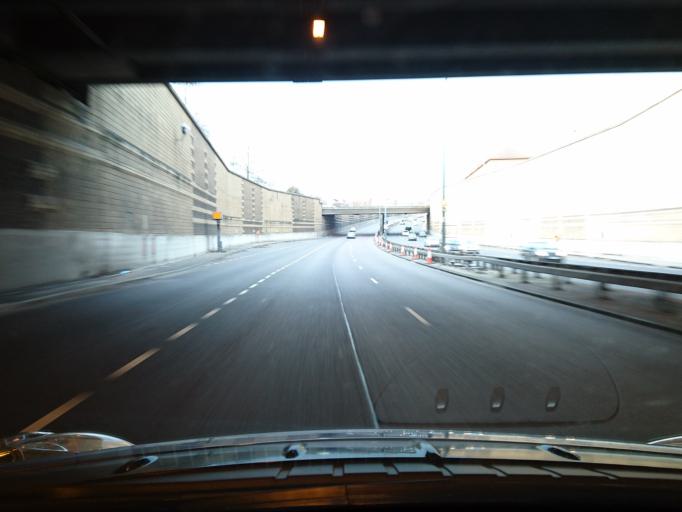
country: GB
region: England
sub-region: Greater London
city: Walthamstow
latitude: 51.5682
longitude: 0.0074
